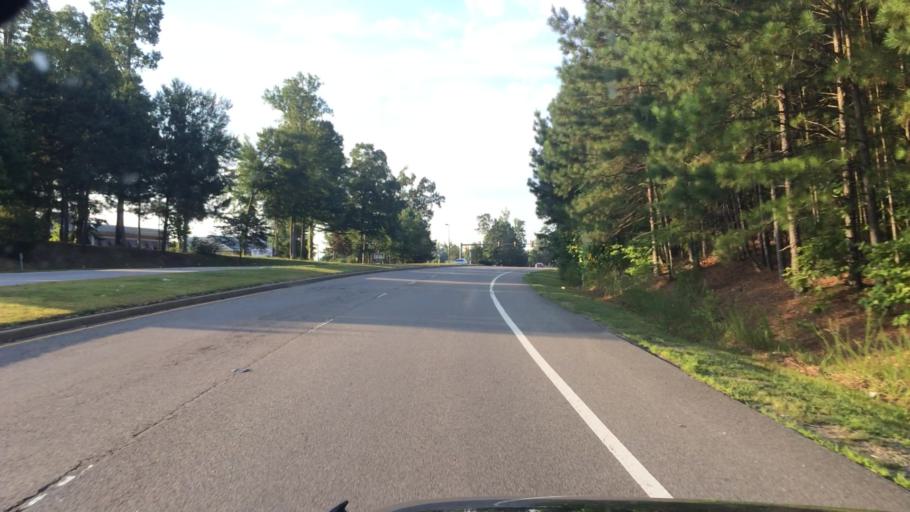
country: US
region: Virginia
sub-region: James City County
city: Williamsburg
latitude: 37.3412
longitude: -76.7392
